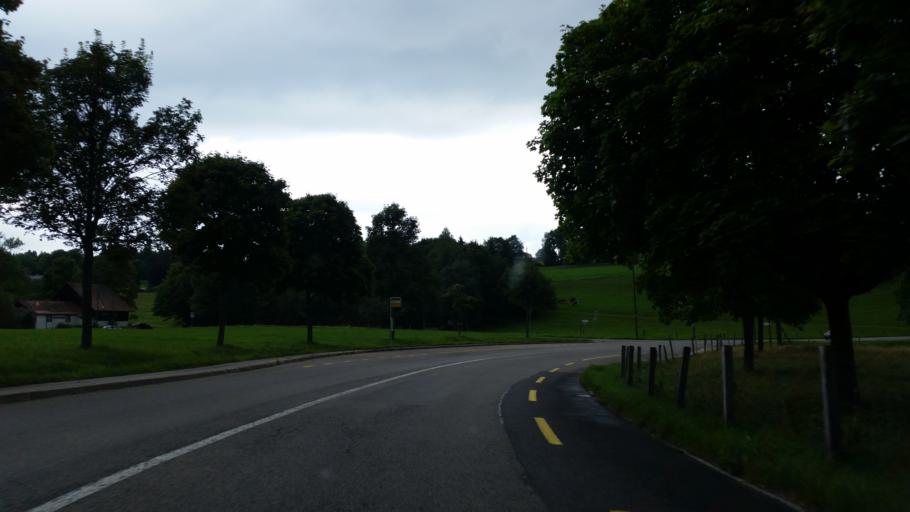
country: CH
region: Neuchatel
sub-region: La Chaux-de-Fonds District
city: La Chaux-de-Fonds
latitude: 47.1166
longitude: 6.8354
